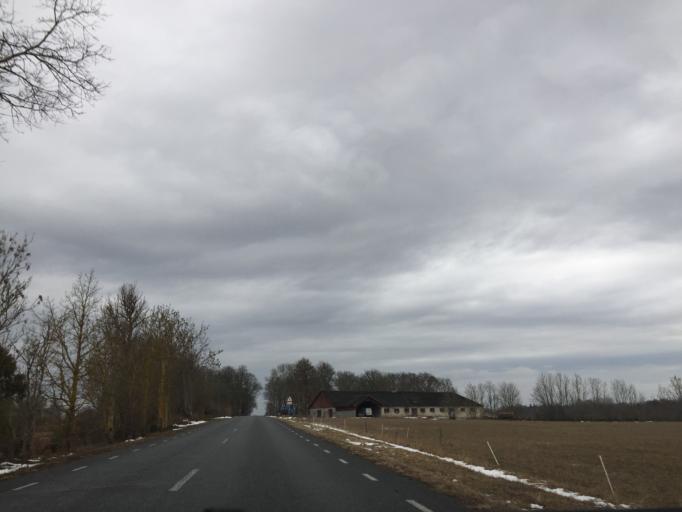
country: EE
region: Saare
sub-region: Orissaare vald
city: Orissaare
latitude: 58.5553
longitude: 22.7746
